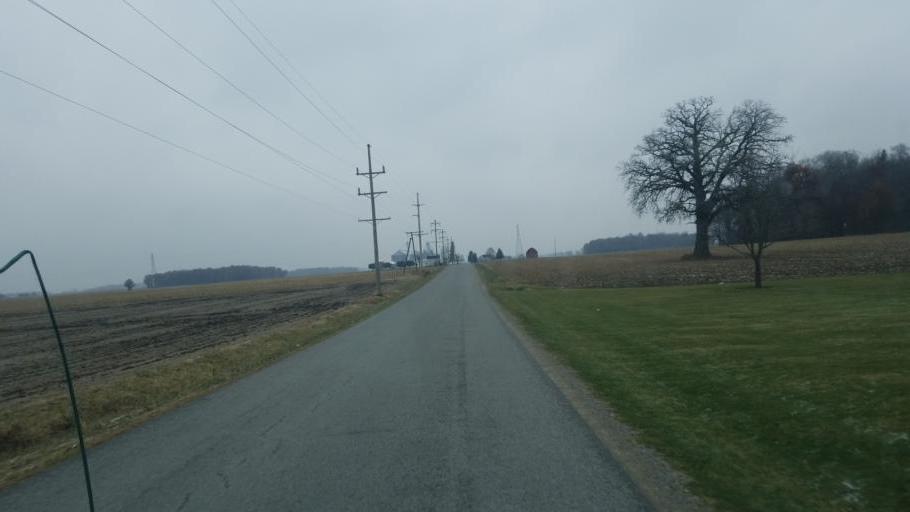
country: US
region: Ohio
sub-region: Crawford County
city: Crestline
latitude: 40.8495
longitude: -82.7297
